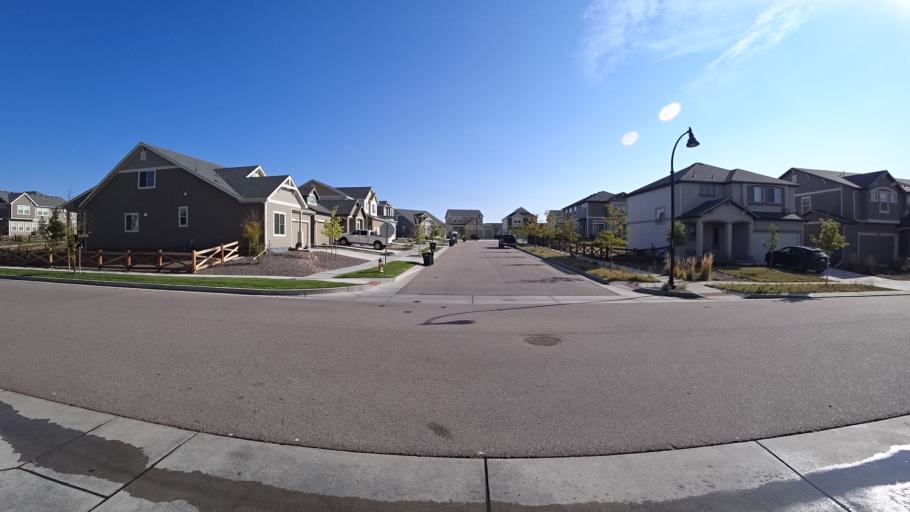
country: US
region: Colorado
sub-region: El Paso County
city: Cimarron Hills
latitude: 38.9324
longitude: -104.6701
